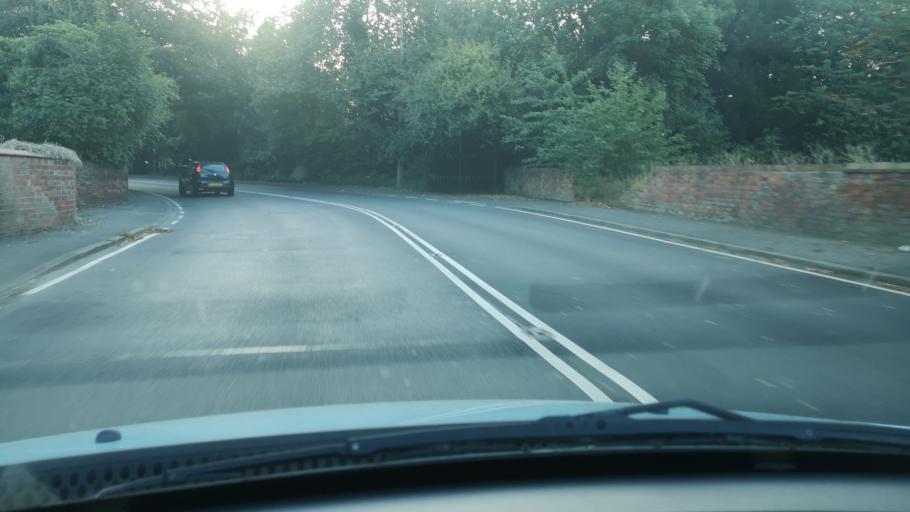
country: GB
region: England
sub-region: Doncaster
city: Hatfield
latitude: 53.5742
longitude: -1.0028
